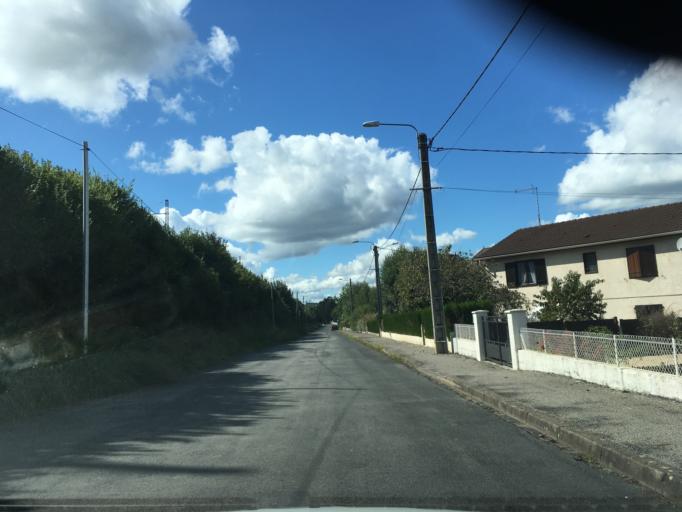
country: FR
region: Limousin
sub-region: Departement de la Correze
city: Brive-la-Gaillarde
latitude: 45.1519
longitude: 1.5011
